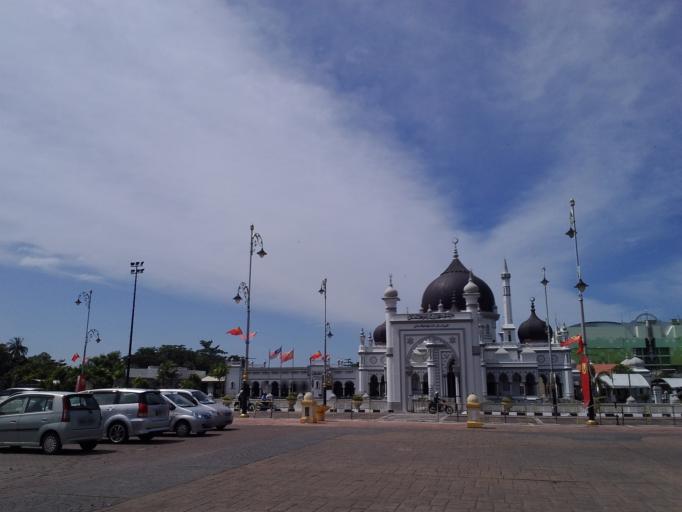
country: MY
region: Kedah
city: Alor Setar
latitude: 6.1200
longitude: 100.3661
